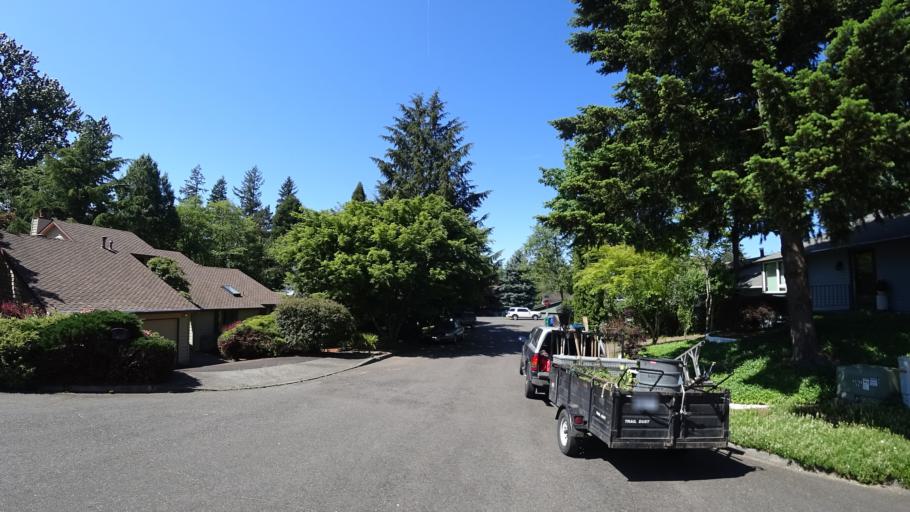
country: US
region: Oregon
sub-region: Washington County
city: Metzger
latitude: 45.4514
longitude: -122.7148
